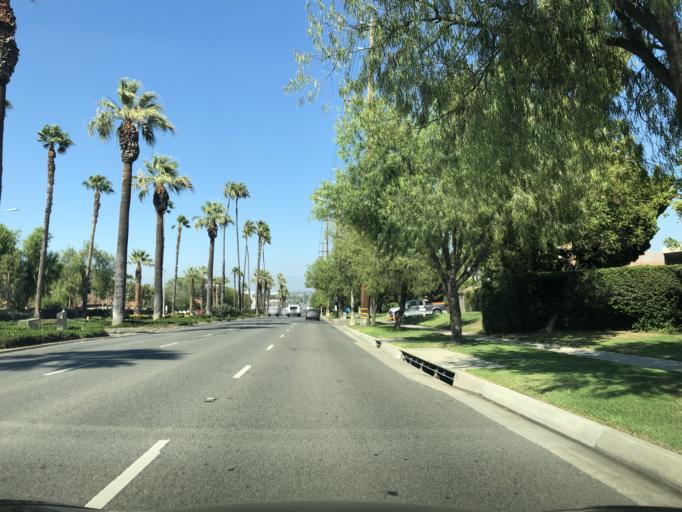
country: US
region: California
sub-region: Riverside County
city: Corona
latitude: 33.8626
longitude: -117.5478
